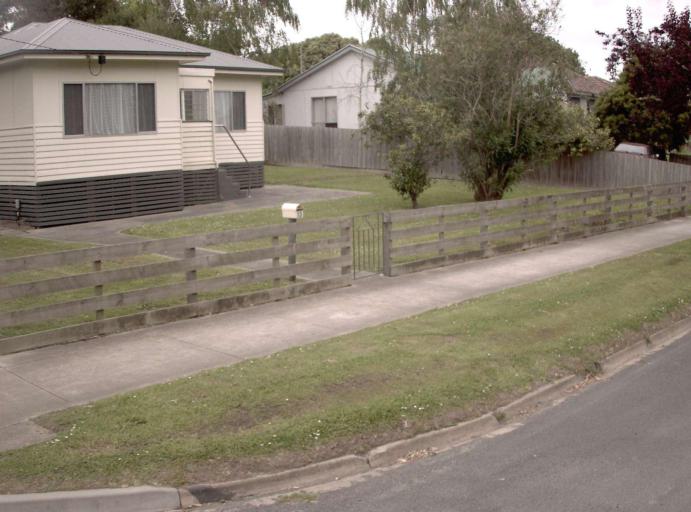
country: AU
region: Victoria
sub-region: Bass Coast
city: North Wonthaggi
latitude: -38.4394
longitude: 145.8284
